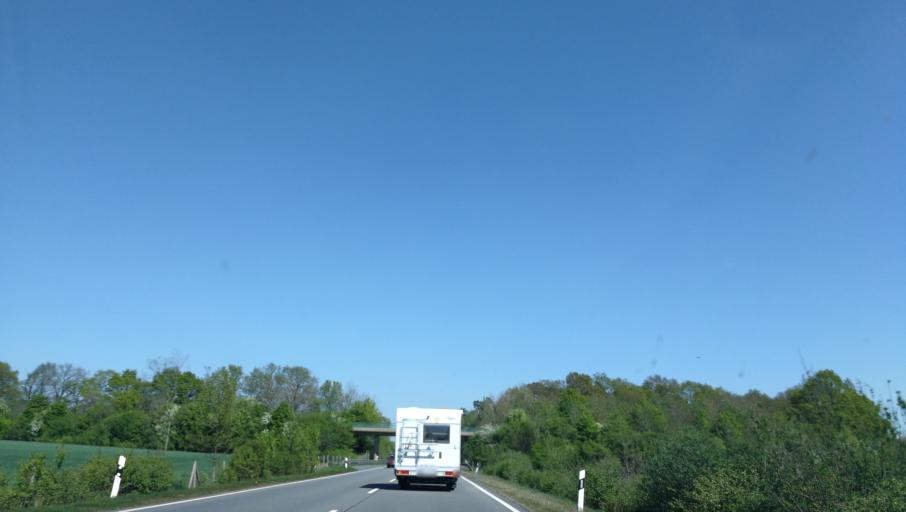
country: DE
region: North Rhine-Westphalia
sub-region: Regierungsbezirk Munster
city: Neuenkirchen
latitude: 52.2304
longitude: 7.3895
